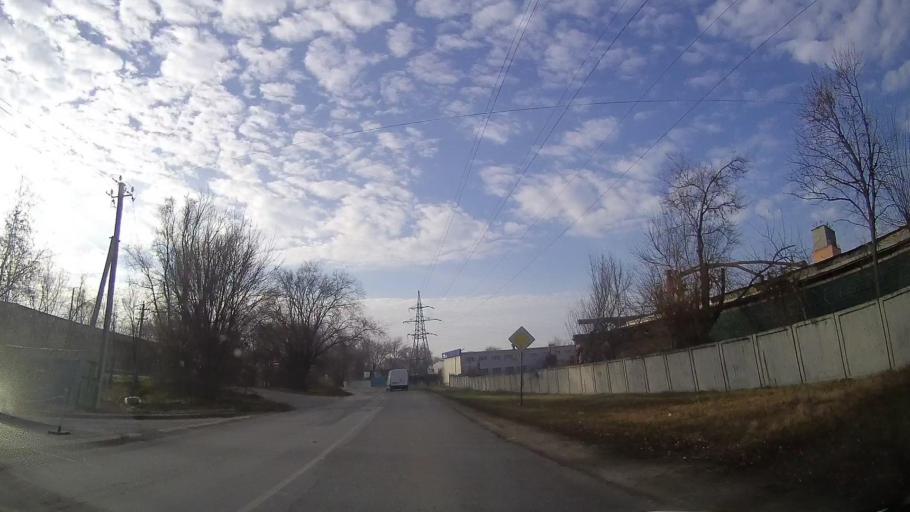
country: RU
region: Rostov
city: Bataysk
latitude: 47.1058
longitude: 39.7630
